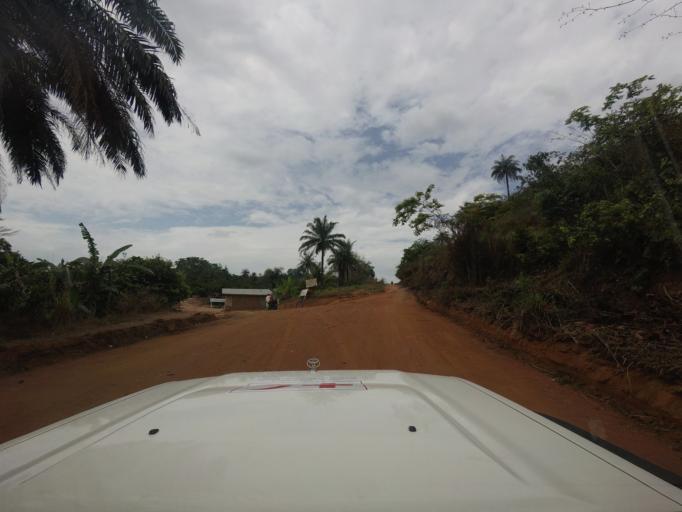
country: SL
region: Eastern Province
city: Buedu
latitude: 8.2789
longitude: -10.2356
